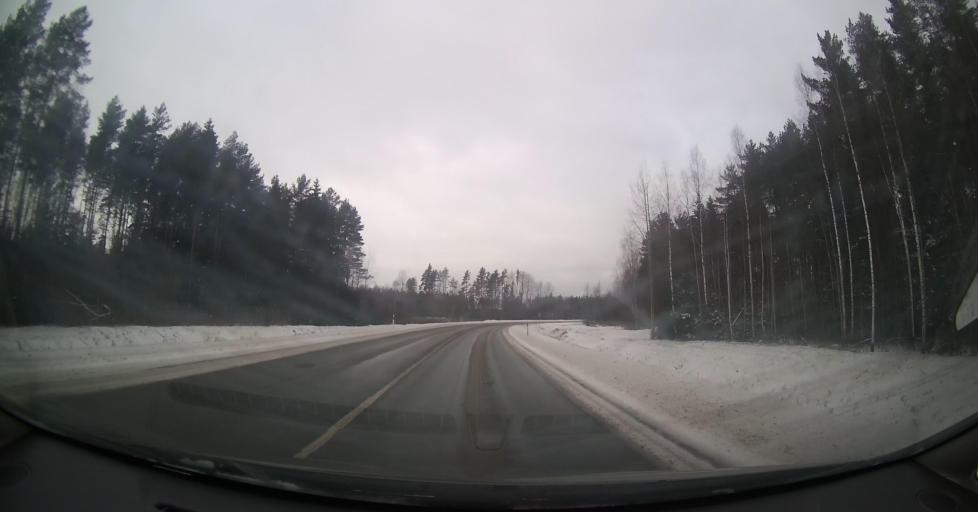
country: EE
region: Harju
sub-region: Raasiku vald
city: Raasiku
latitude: 59.4279
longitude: 25.1968
